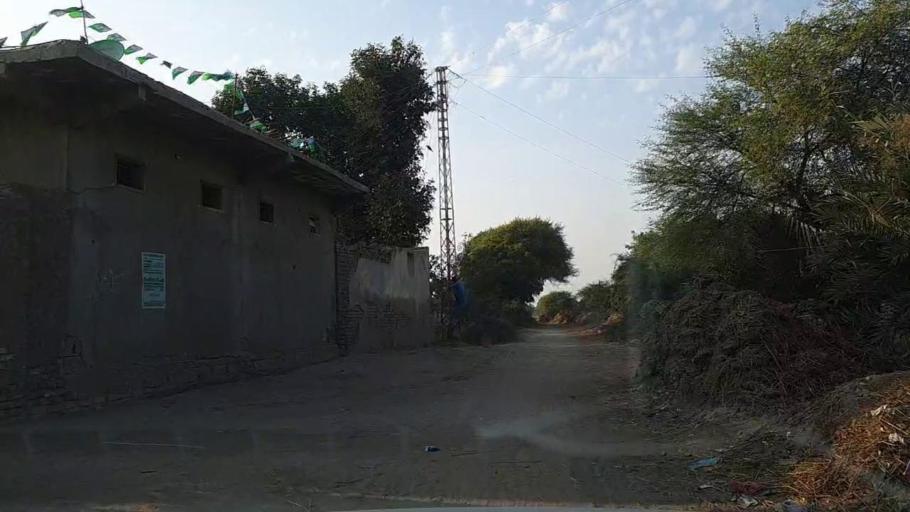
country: PK
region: Sindh
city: Daro Mehar
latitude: 24.7731
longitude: 68.1993
